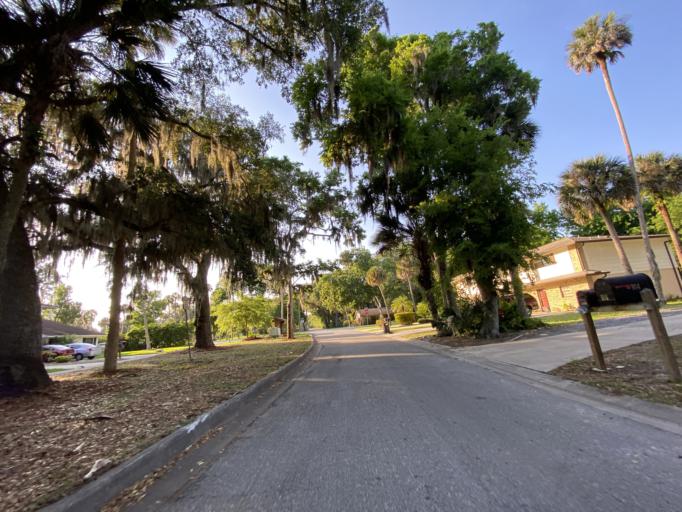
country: US
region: Florida
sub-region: Volusia County
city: Port Orange
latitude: 29.1464
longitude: -81.0084
